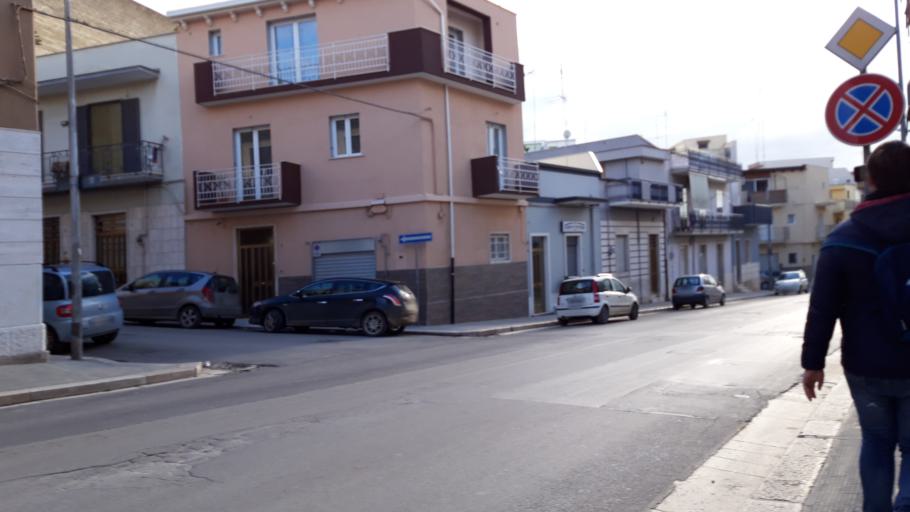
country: IT
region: Apulia
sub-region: Provincia di Barletta - Andria - Trani
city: Andria
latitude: 41.2317
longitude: 16.2889
